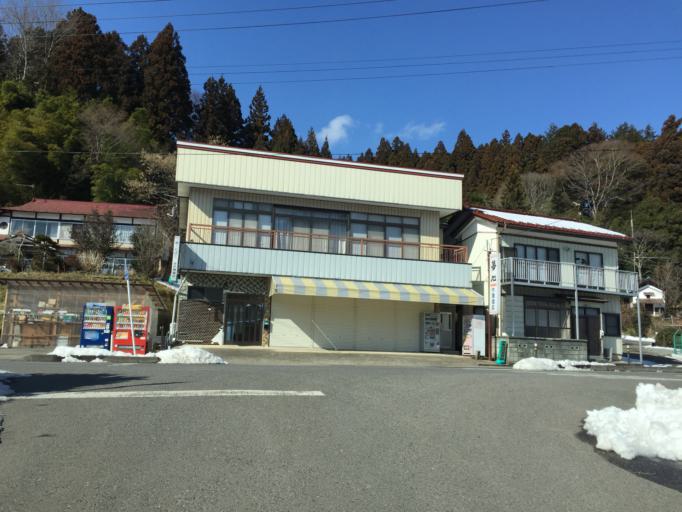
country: JP
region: Fukushima
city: Miharu
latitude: 37.2933
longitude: 140.5385
